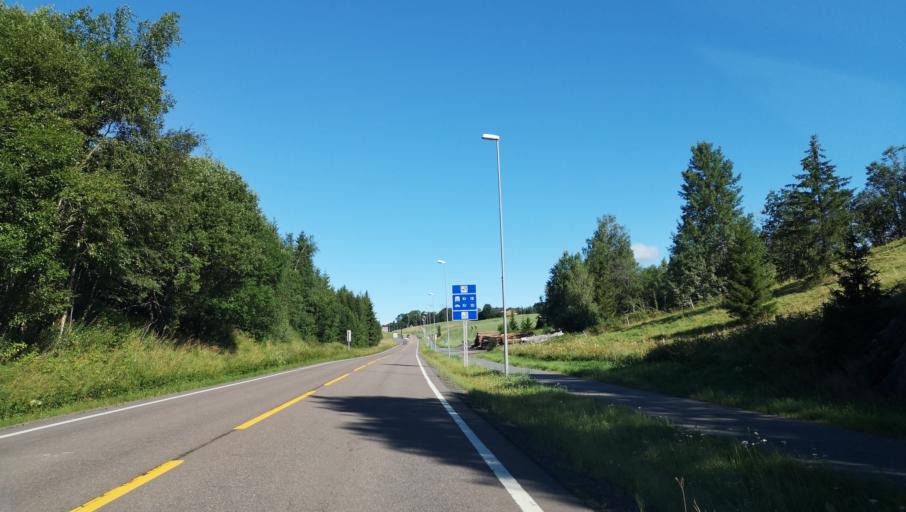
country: NO
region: Ostfold
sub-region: Spydeberg
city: Spydeberg
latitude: 59.6061
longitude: 11.0994
